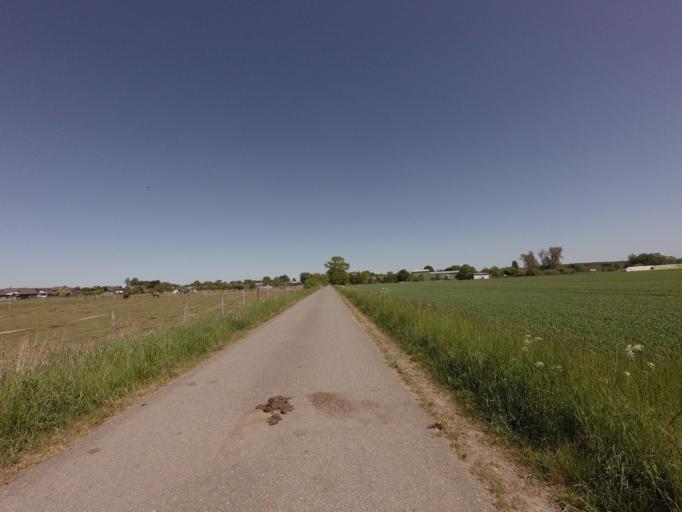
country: DE
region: Lower Saxony
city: Lehre
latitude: 52.3071
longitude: 10.5974
